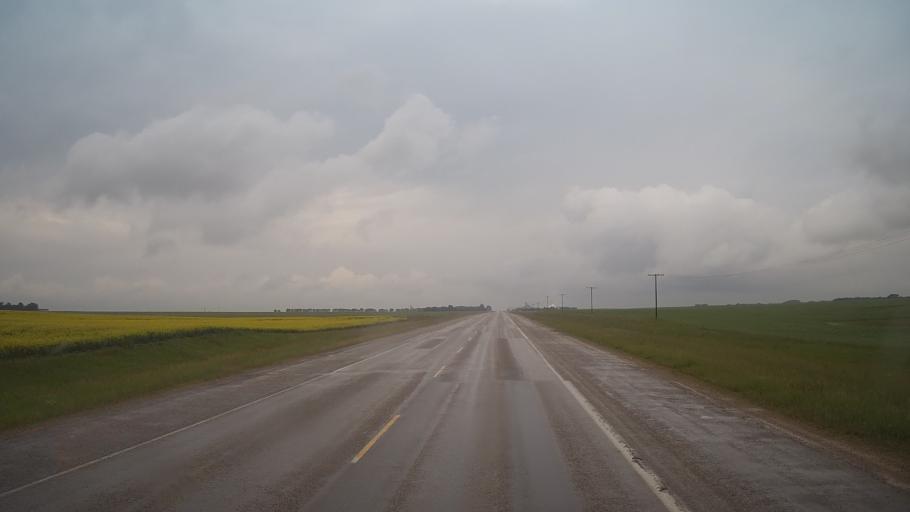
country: CA
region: Saskatchewan
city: Unity
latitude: 52.4350
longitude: -109.0581
